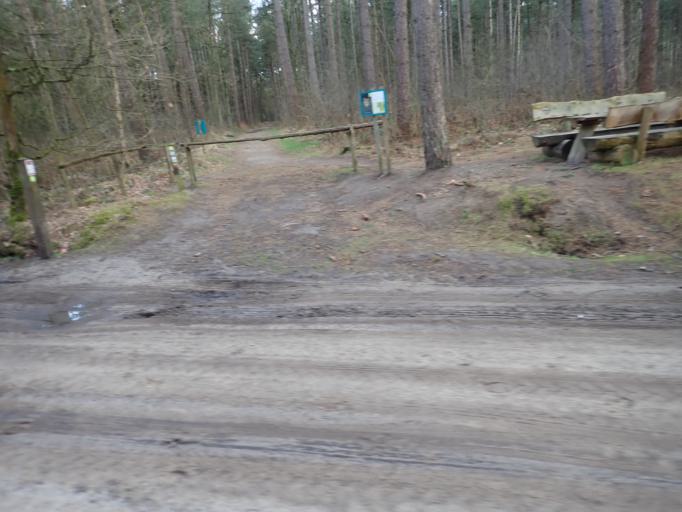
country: BE
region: Flanders
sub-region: Provincie Antwerpen
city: Grobbendonk
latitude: 51.2250
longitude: 4.7420
